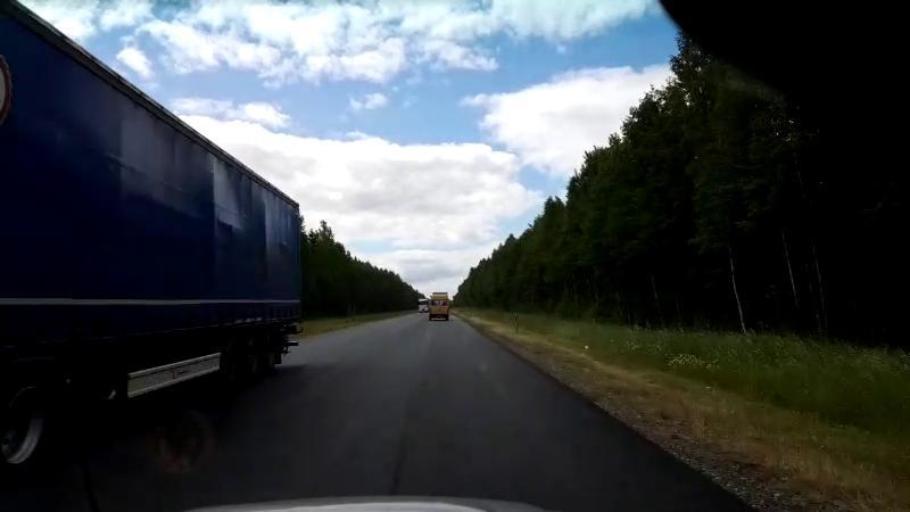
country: LV
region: Salacgrivas
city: Ainazi
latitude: 57.9202
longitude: 24.4225
